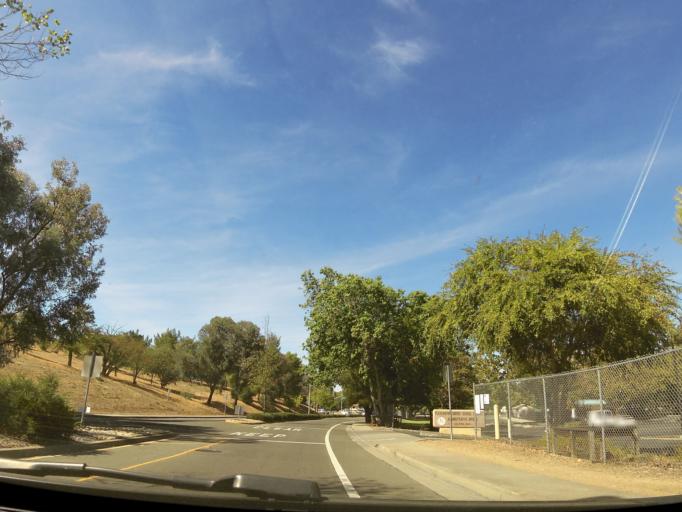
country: US
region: California
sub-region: Alameda County
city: Pleasanton
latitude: 37.6554
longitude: -121.8759
